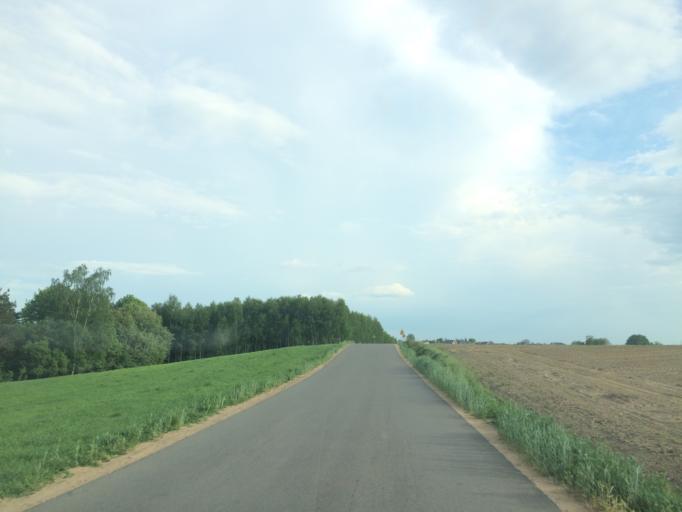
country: PL
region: Kujawsko-Pomorskie
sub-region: Powiat brodnicki
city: Brzozie
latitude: 53.3666
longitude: 19.7102
